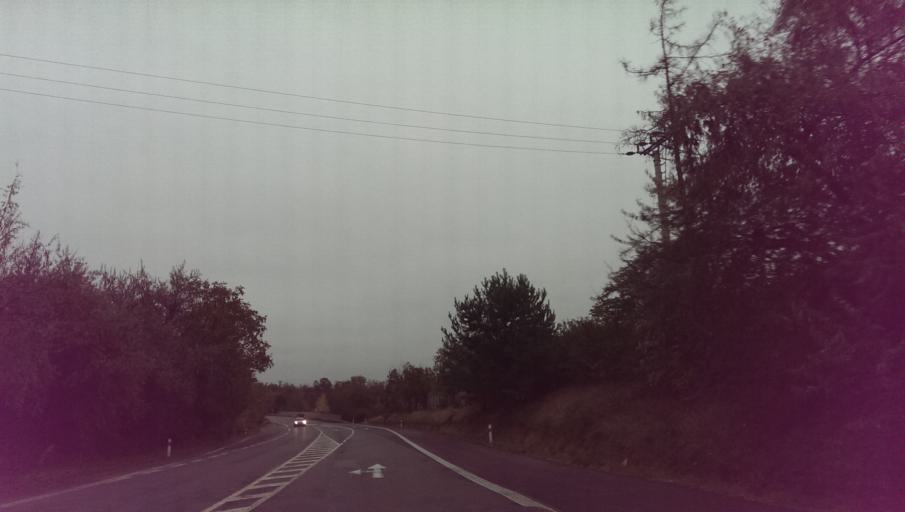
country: CZ
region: South Moravian
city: Dobsice
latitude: 48.8521
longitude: 16.0868
